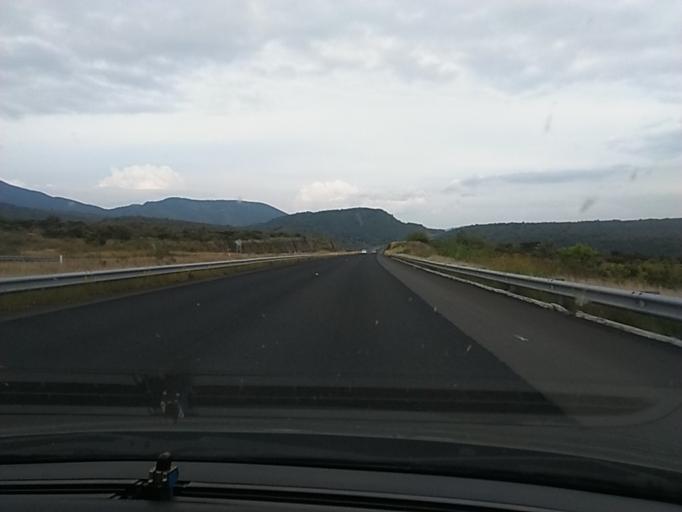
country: MX
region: Mexico
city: Huaniqueo de Morales
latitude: 19.8866
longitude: -101.4759
